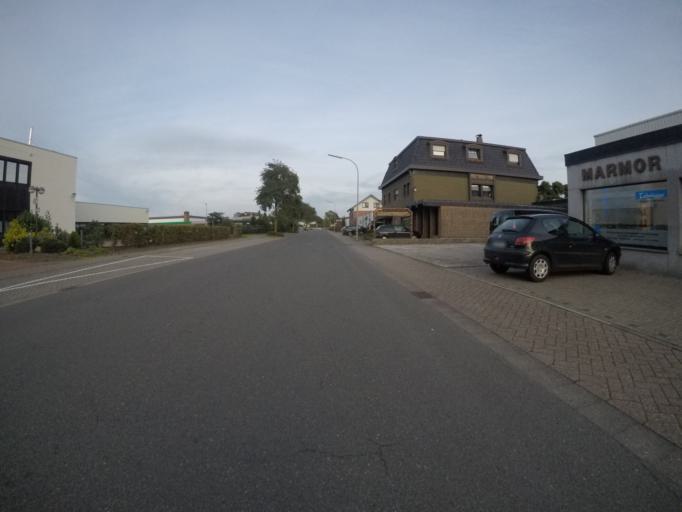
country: DE
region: North Rhine-Westphalia
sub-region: Regierungsbezirk Munster
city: Rhede
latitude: 51.8307
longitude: 6.7083
